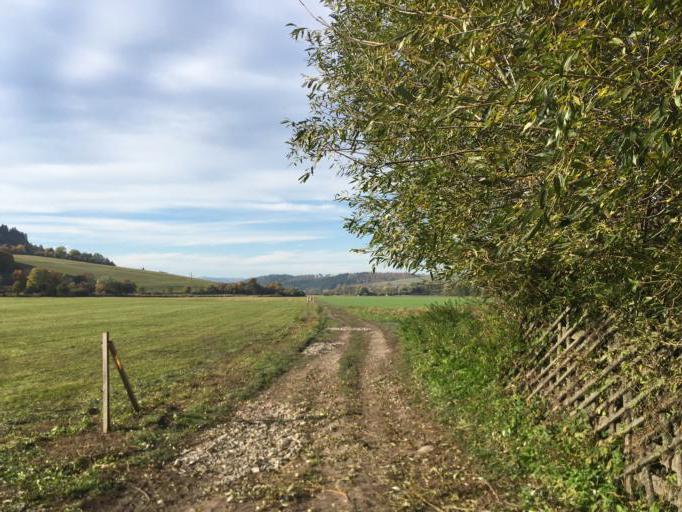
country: SK
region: Trenciansky
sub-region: Okres Povazska Bystrica
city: Povazska Bystrica
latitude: 49.0381
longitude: 18.4333
